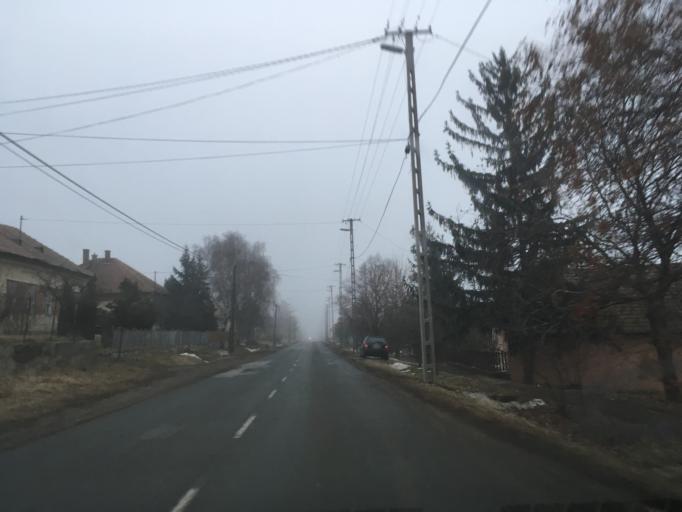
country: HU
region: Heves
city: Kerecsend
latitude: 47.7923
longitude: 20.3500
